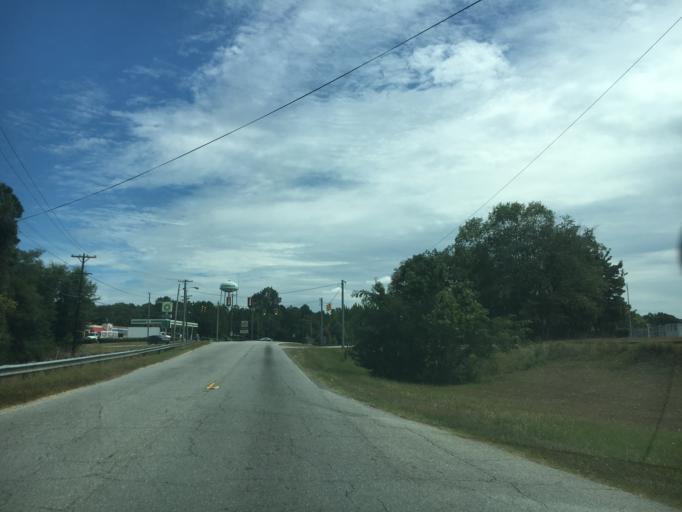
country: US
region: South Carolina
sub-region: Laurens County
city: Laurens
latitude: 34.5271
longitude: -82.0451
